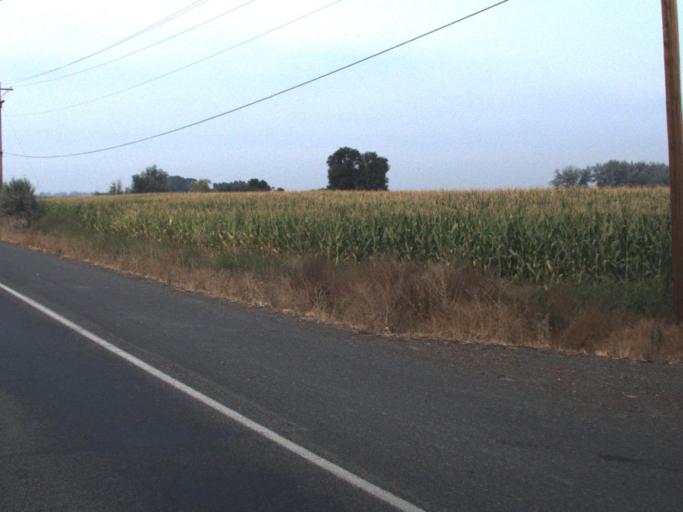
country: US
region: Washington
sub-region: Yakima County
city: Granger
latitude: 46.3277
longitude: -120.2382
